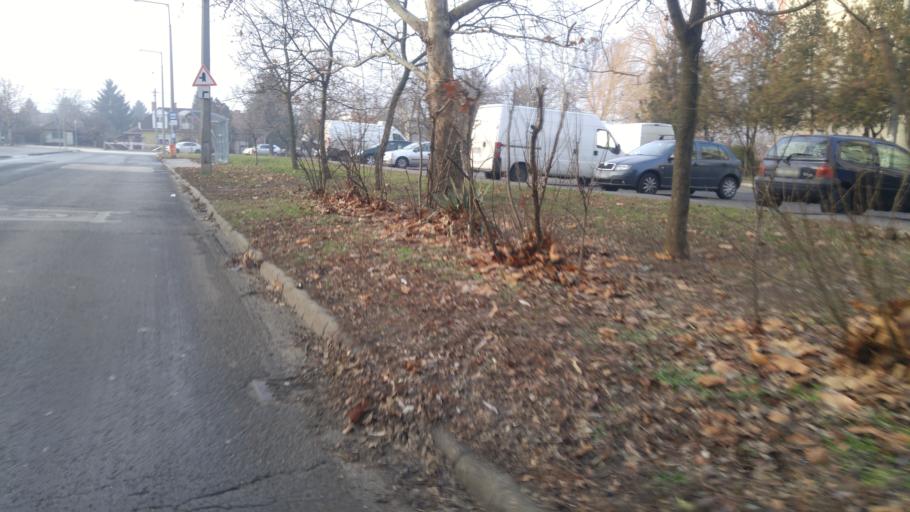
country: HU
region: Budapest
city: Budapest XVII. keruelet
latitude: 47.4795
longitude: 19.2336
